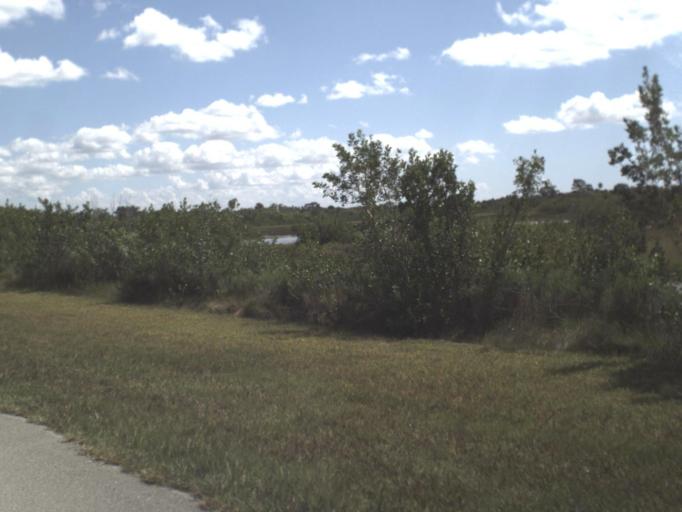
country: US
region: Florida
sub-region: Collier County
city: Marco
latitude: 25.9604
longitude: -81.4944
